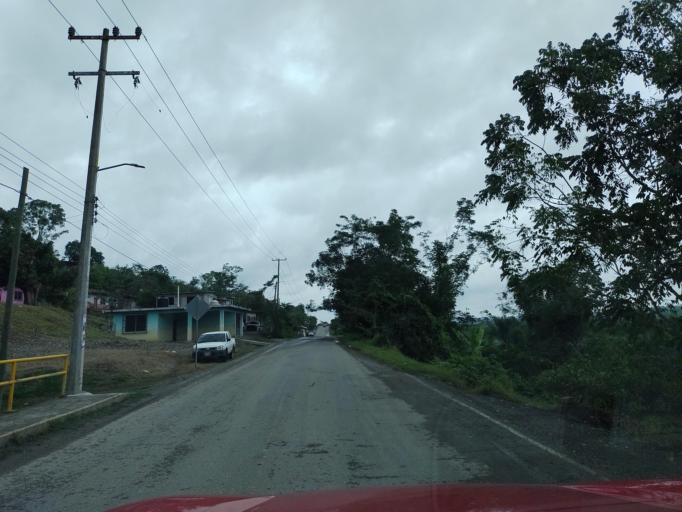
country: MX
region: Puebla
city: Espinal
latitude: 20.2622
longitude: -97.3704
